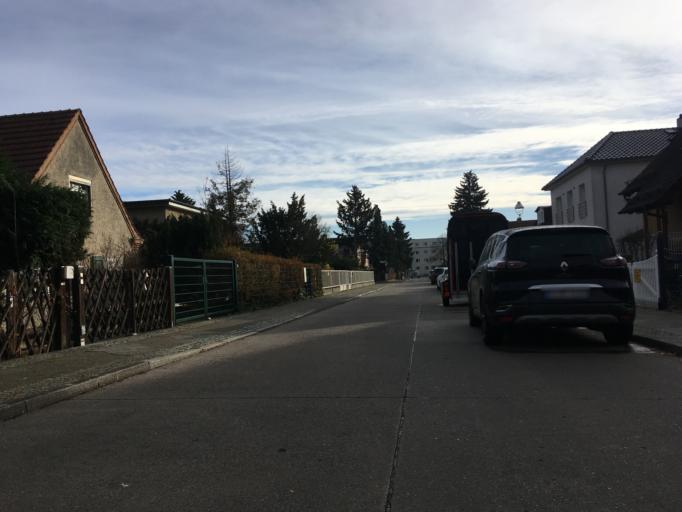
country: DE
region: Berlin
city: Rudow
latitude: 52.4311
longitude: 13.4908
